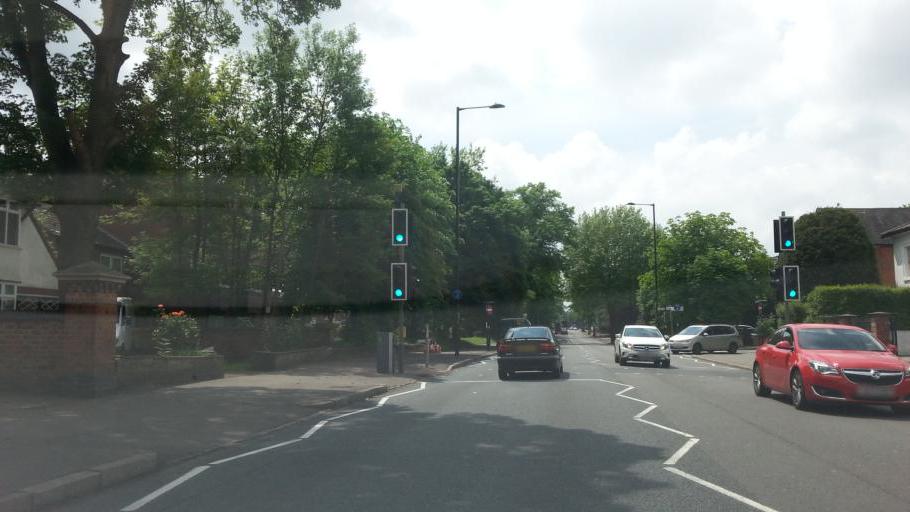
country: GB
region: England
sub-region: City and Borough of Birmingham
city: Birmingham
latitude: 52.4591
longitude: -1.9073
